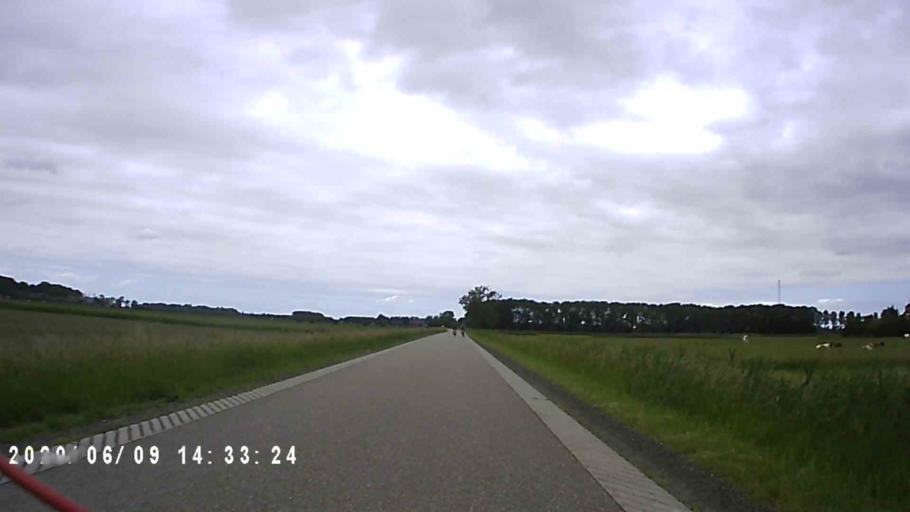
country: NL
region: Groningen
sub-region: Gemeente Bedum
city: Bedum
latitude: 53.3229
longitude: 6.5909
